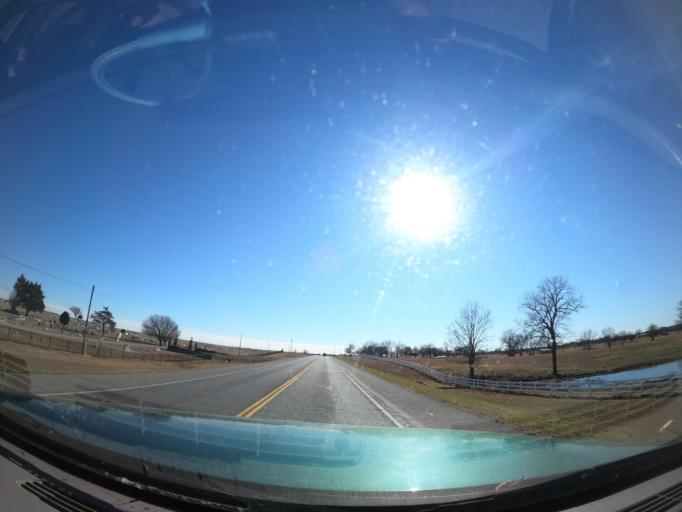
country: US
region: Oklahoma
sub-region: Muskogee County
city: Haskell
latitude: 35.8381
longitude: -95.6777
